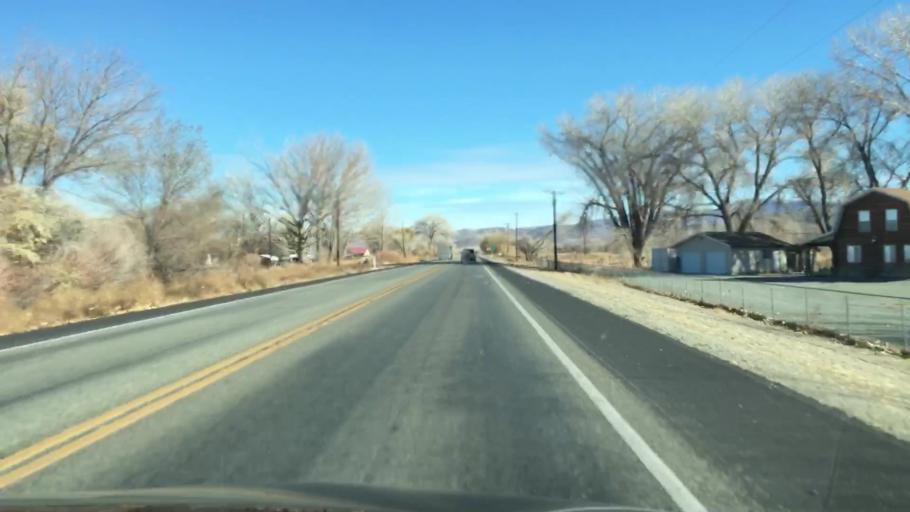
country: US
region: Nevada
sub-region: Lyon County
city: Yerington
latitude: 38.9975
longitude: -119.1461
